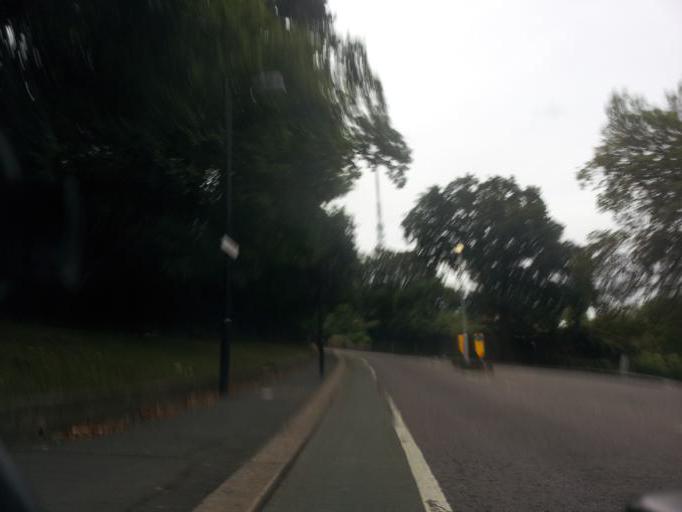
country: GB
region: England
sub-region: Greater London
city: Thornton Heath
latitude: 51.4290
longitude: -0.0779
